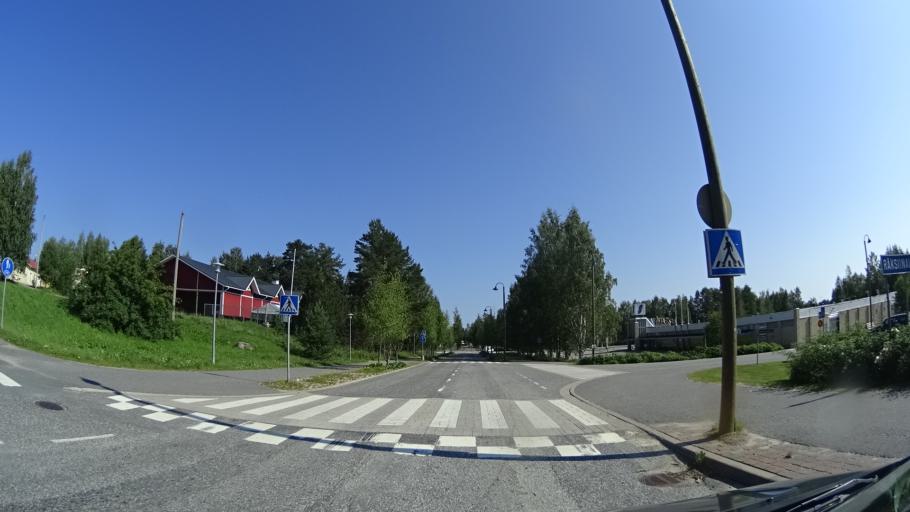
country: FI
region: North Karelia
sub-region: Joensuu
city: Juuka
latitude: 63.2403
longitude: 29.2515
